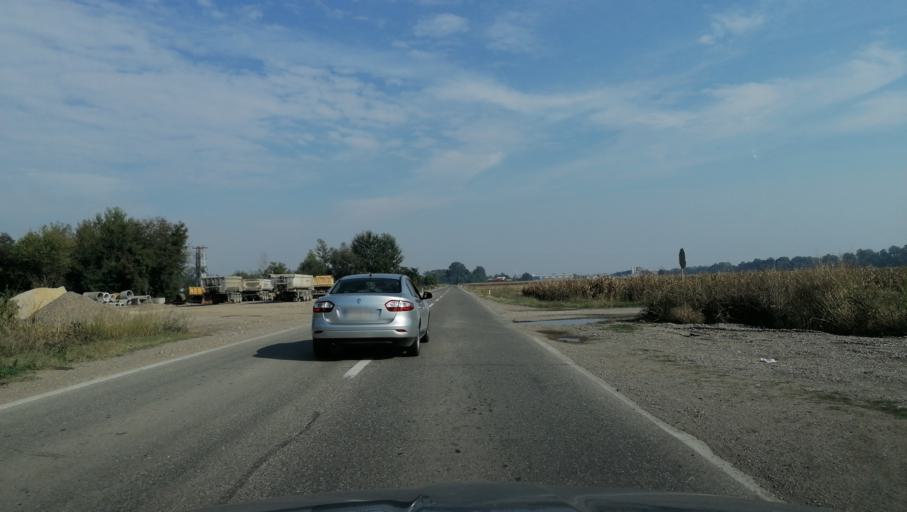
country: BA
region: Republika Srpska
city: Popovi
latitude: 44.7811
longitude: 19.2983
